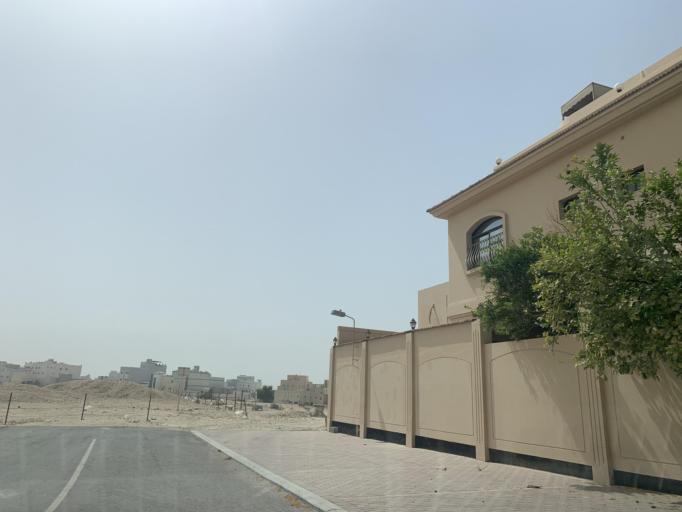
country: BH
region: Northern
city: Madinat `Isa
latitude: 26.1549
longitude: 50.5147
